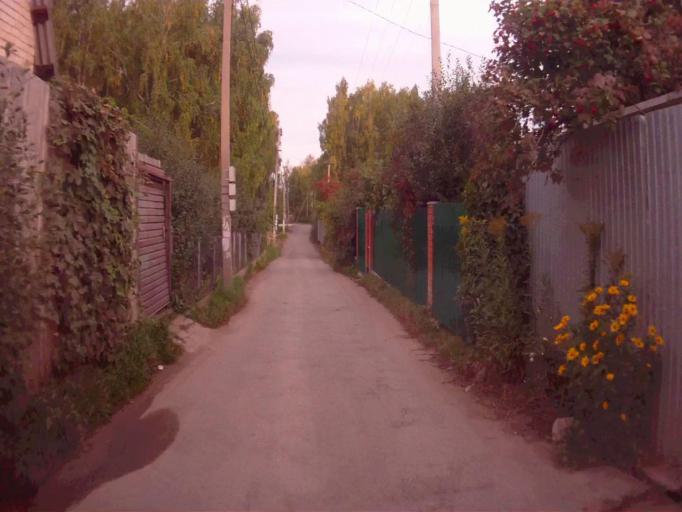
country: RU
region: Chelyabinsk
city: Sargazy
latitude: 55.1323
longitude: 61.2489
